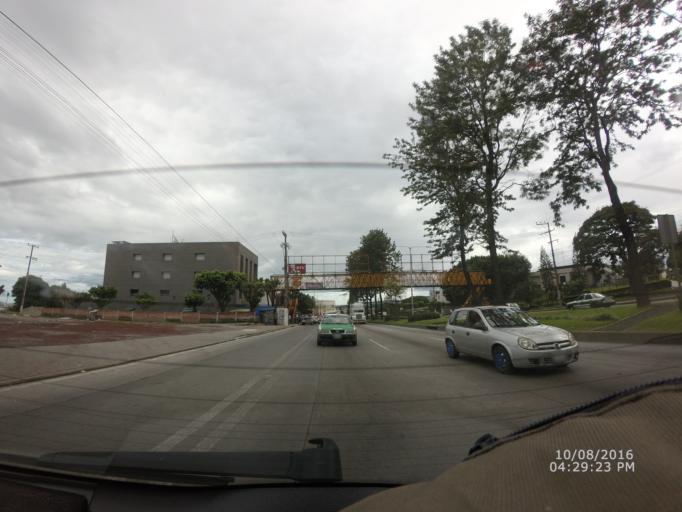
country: MX
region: Veracruz
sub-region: Xalapa
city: Xalapa de Enriquez
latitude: 19.5428
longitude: -96.9087
